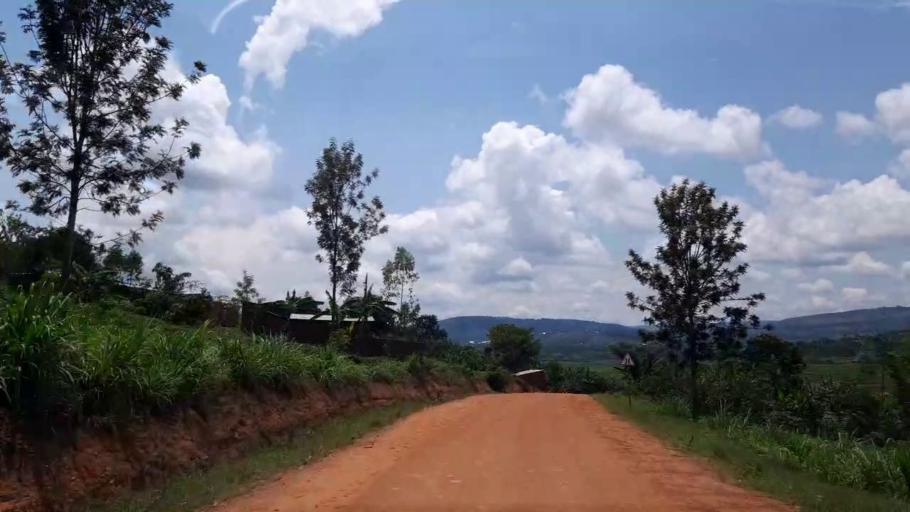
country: RW
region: Northern Province
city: Byumba
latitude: -1.5698
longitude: 30.2951
